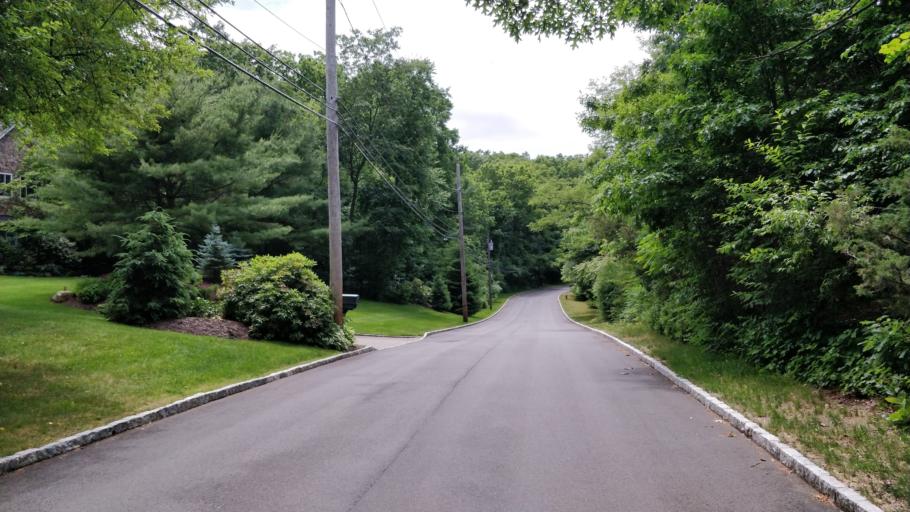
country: US
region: New York
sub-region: Nassau County
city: Laurel Hollow
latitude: 40.8414
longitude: -73.4699
